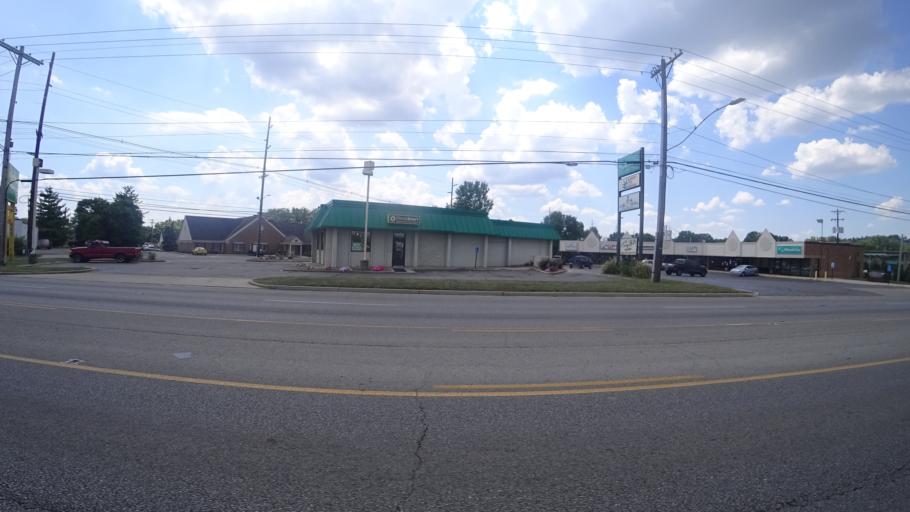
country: US
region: Ohio
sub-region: Butler County
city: Hamilton
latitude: 39.4211
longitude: -84.5907
